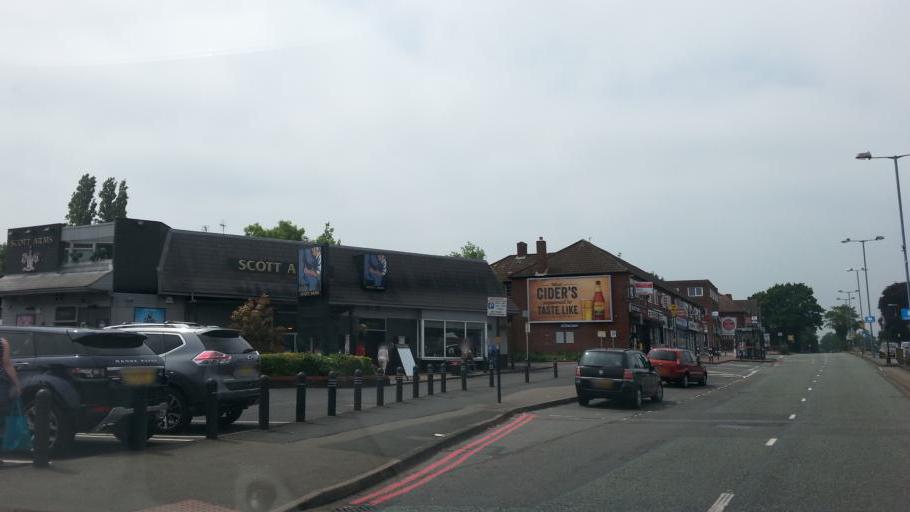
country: GB
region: England
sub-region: City and Borough of Birmingham
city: Hockley
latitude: 52.5458
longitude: -1.9334
